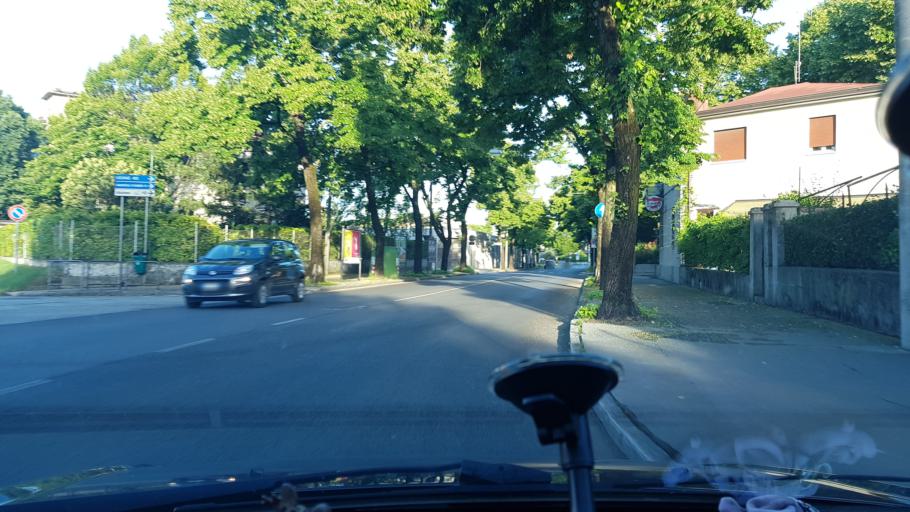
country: IT
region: Friuli Venezia Giulia
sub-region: Provincia di Gorizia
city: Gorizia
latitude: 45.9348
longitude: 13.6111
